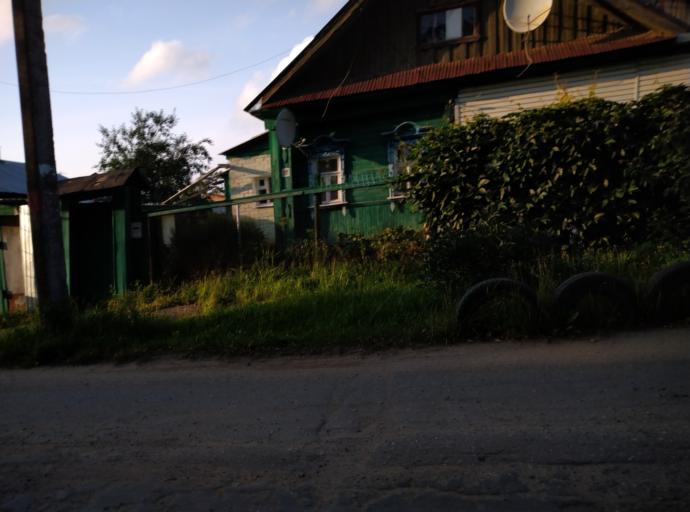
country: RU
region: Kostroma
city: Oktyabr'skiy
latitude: 57.7505
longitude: 40.9690
